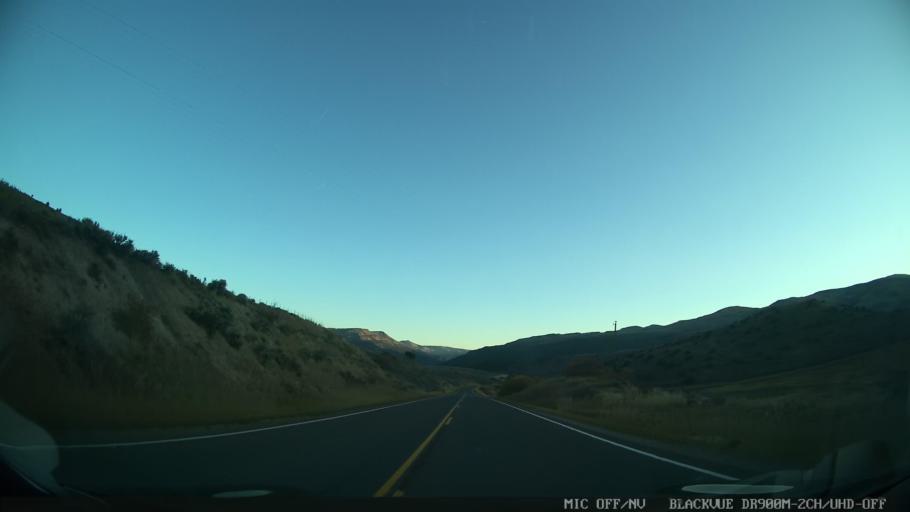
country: US
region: Colorado
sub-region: Eagle County
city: Edwards
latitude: 39.8234
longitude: -106.6425
